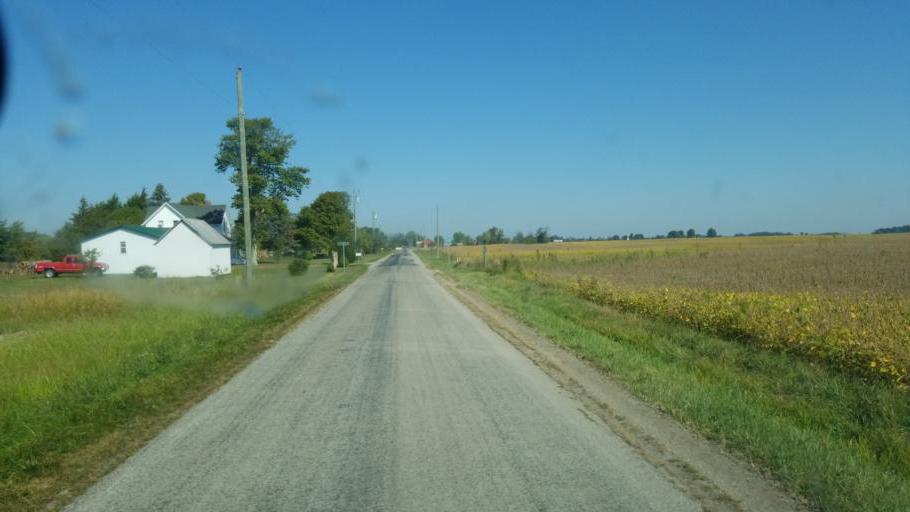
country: US
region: Ohio
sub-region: Union County
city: Richwood
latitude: 40.5045
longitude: -83.4365
